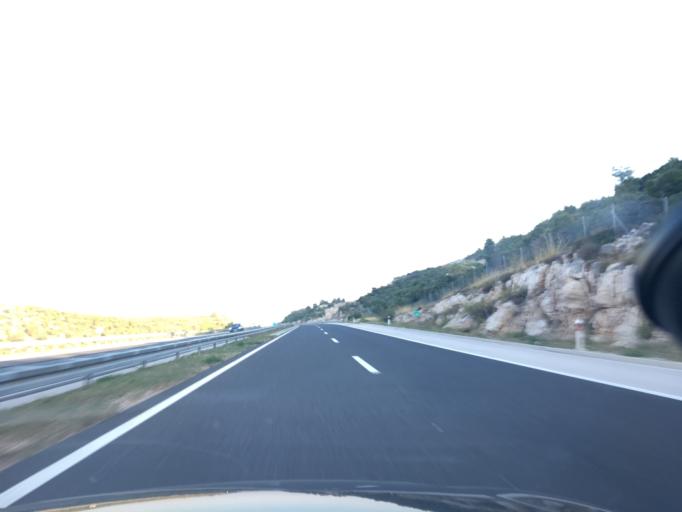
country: HR
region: Sibensko-Kniniska
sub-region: Grad Sibenik
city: Sibenik
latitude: 43.7562
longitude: 15.9420
